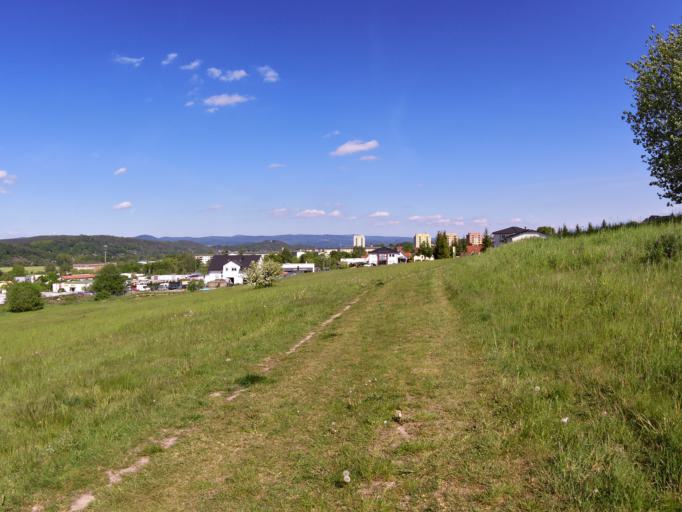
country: DE
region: Thuringia
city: Leimbach
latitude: 50.8098
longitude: 10.2074
